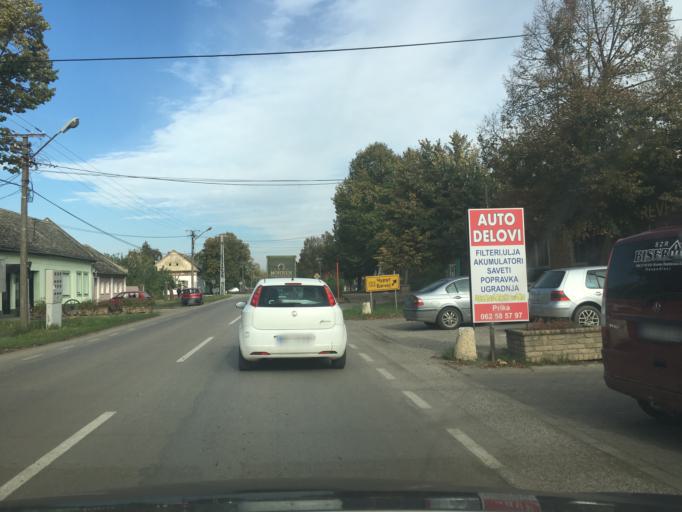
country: RS
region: Autonomna Pokrajina Vojvodina
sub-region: Juznobacki Okrug
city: Zabalj
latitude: 45.3764
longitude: 20.0621
